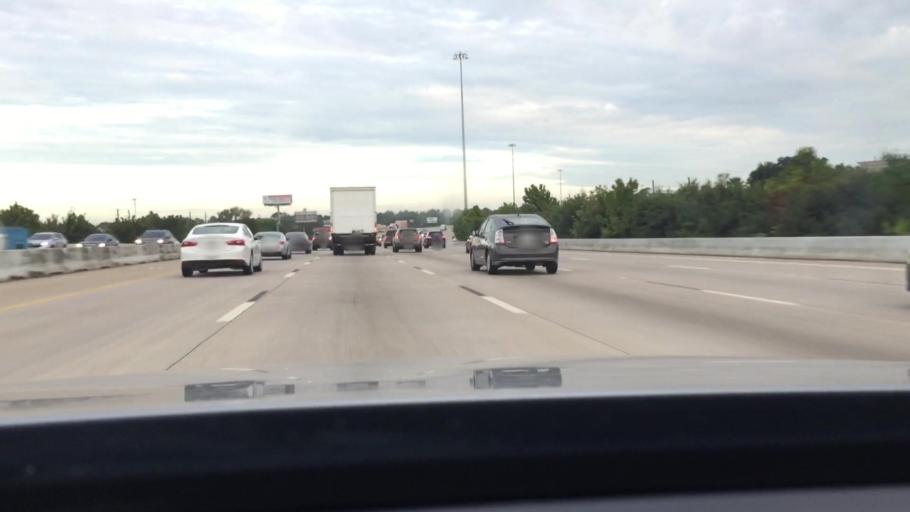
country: US
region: Texas
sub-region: Harris County
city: Oak Cliff Place
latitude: 29.9678
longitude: -95.5576
